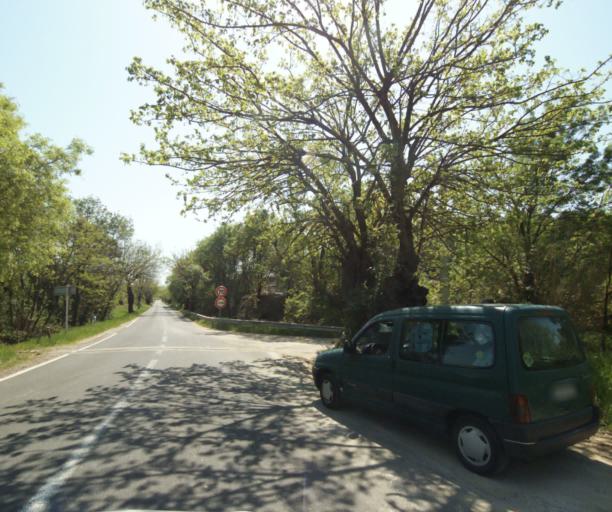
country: FR
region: Languedoc-Roussillon
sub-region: Departement de l'Herault
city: Saint-Clement-de-Riviere
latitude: 43.6580
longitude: 3.8303
